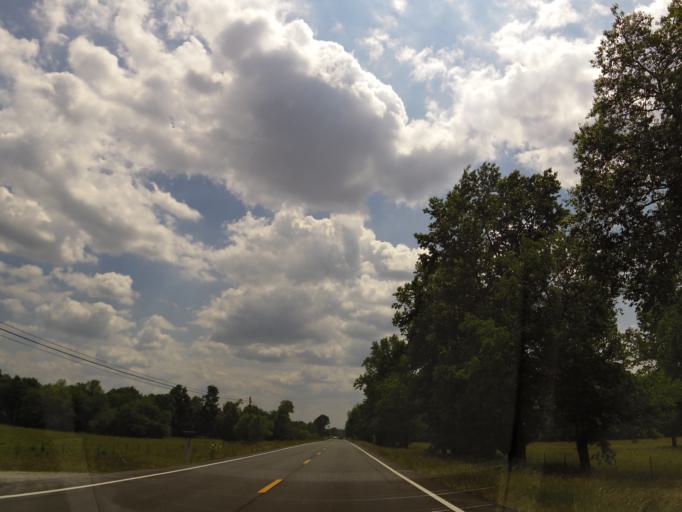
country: US
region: Tennessee
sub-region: Sequatchie County
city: Dunlap
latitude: 35.4743
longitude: -85.3165
